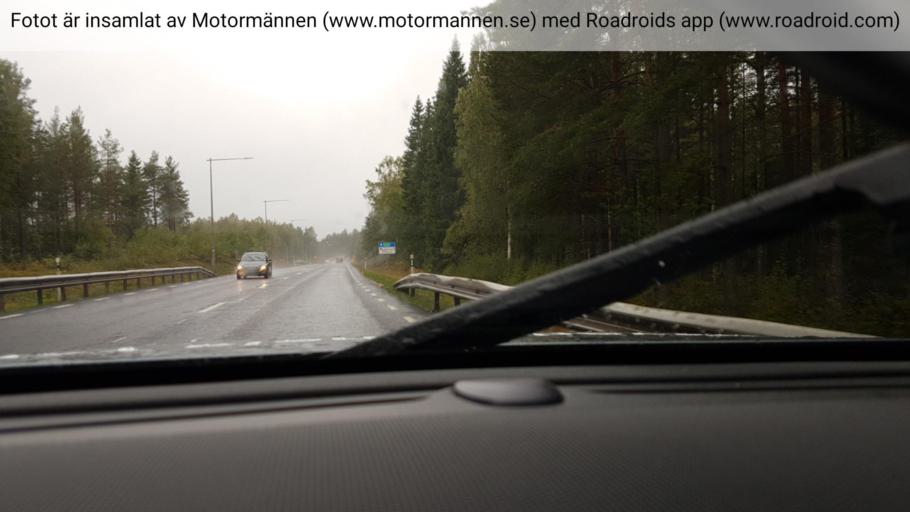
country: SE
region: Vaestra Goetaland
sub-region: Amals Kommun
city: Amal
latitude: 59.0414
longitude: 12.6762
